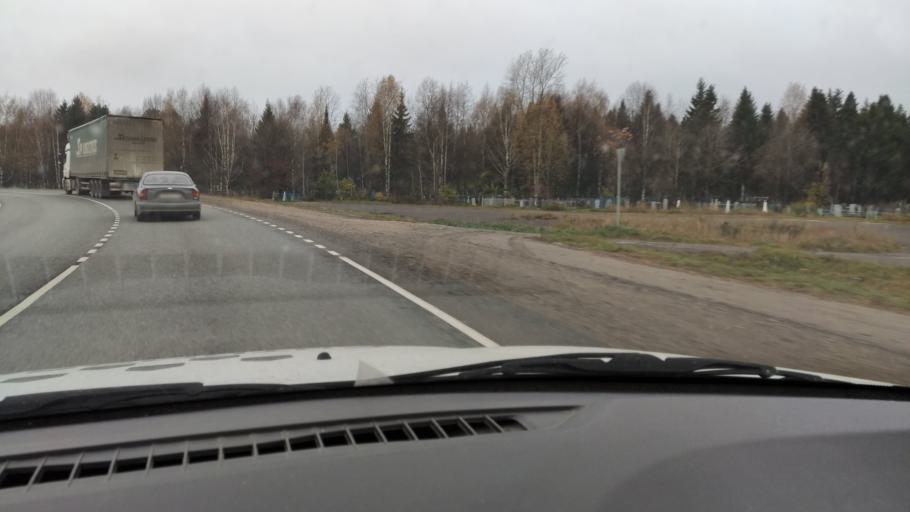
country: RU
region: Kirov
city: Omutninsk
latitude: 58.6933
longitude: 52.1994
